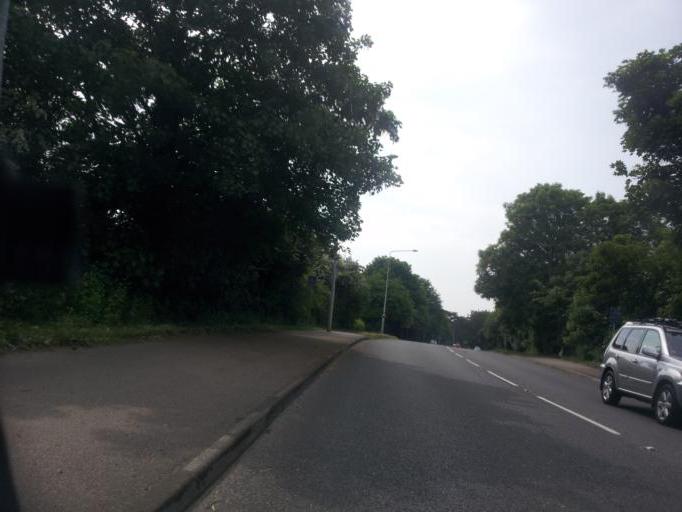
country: GB
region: England
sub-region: Kent
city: West Malling
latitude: 51.2988
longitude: 0.4150
